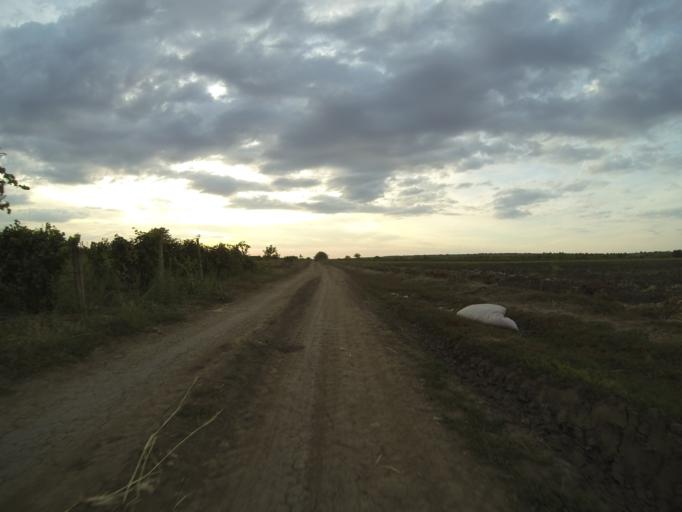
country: RO
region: Dolj
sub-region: Comuna Ceratu
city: Ceratu
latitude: 44.0985
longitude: 23.6867
